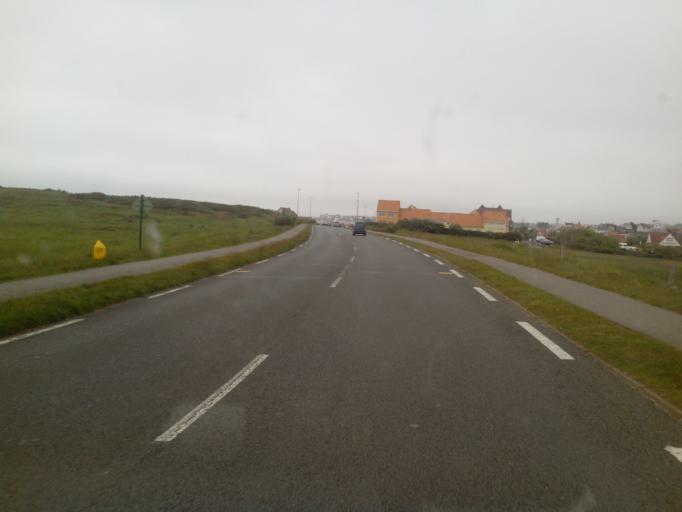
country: FR
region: Nord-Pas-de-Calais
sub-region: Departement du Pas-de-Calais
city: Wimereux
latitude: 50.7586
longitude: 1.6059
